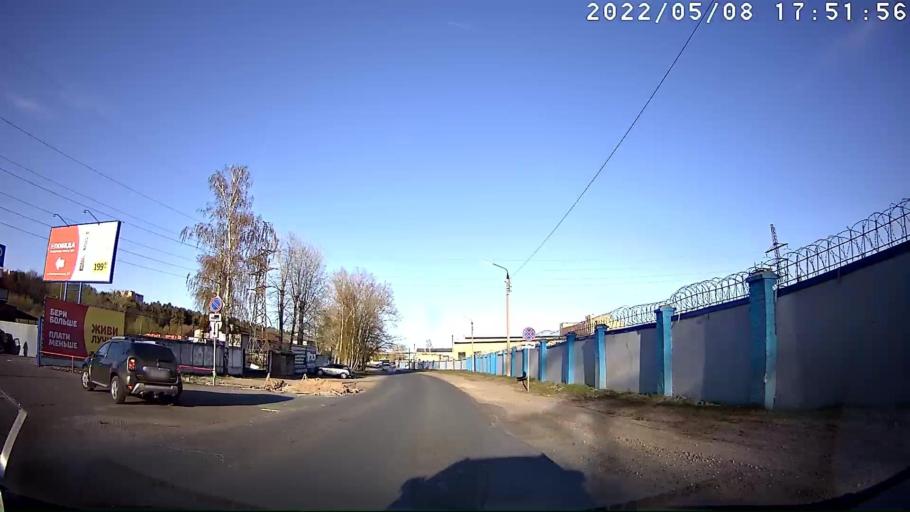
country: RU
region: Tatarstan
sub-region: Zelenodol'skiy Rayon
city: Zelenodolsk
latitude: 55.8406
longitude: 48.4992
